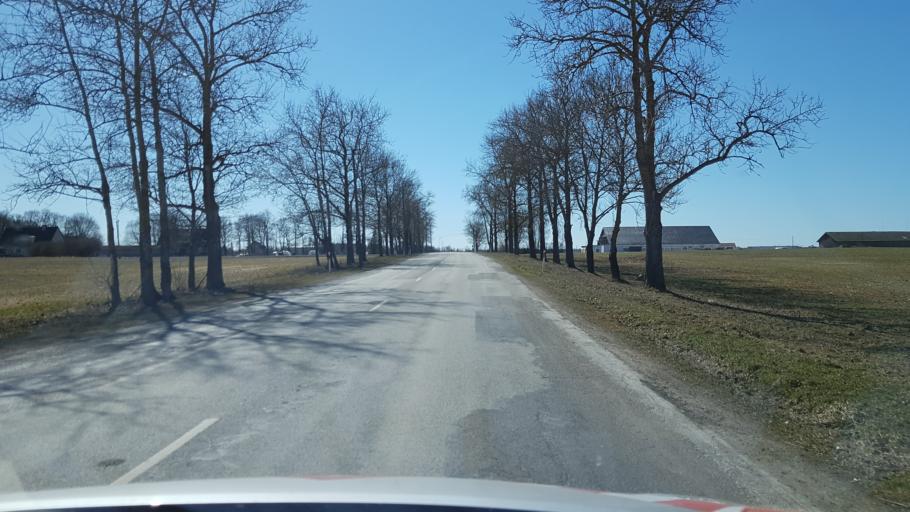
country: EE
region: Laeaene-Virumaa
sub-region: Rakvere linn
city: Rakvere
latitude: 59.3679
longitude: 26.3758
